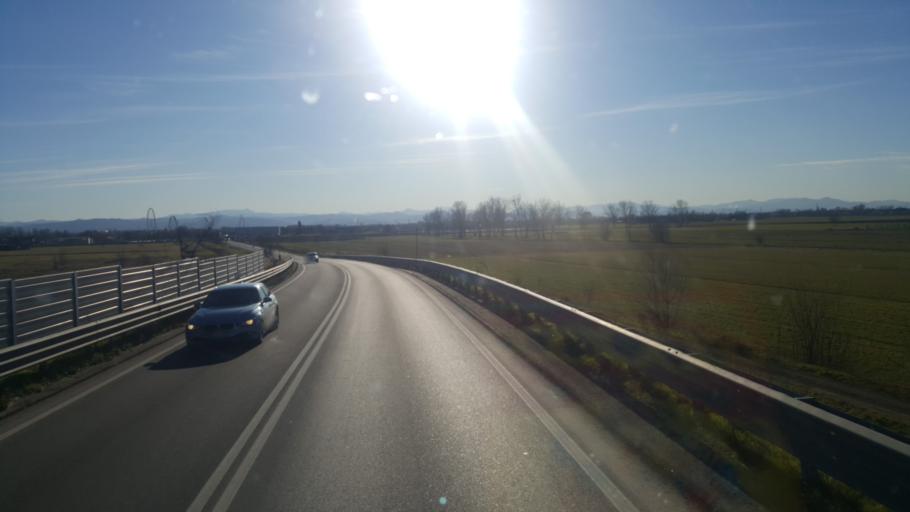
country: IT
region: Emilia-Romagna
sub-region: Provincia di Reggio Emilia
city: Argine
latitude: 44.7456
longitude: 10.6448
